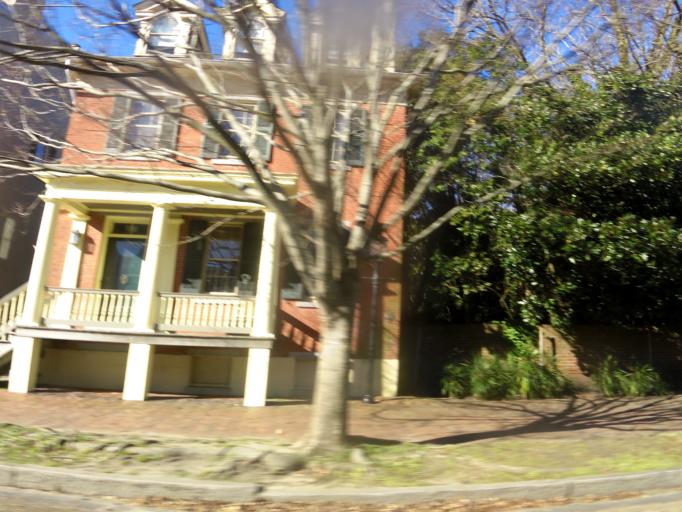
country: US
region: Virginia
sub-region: City of Portsmouth
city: Portsmouth
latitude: 36.8389
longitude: -76.3011
